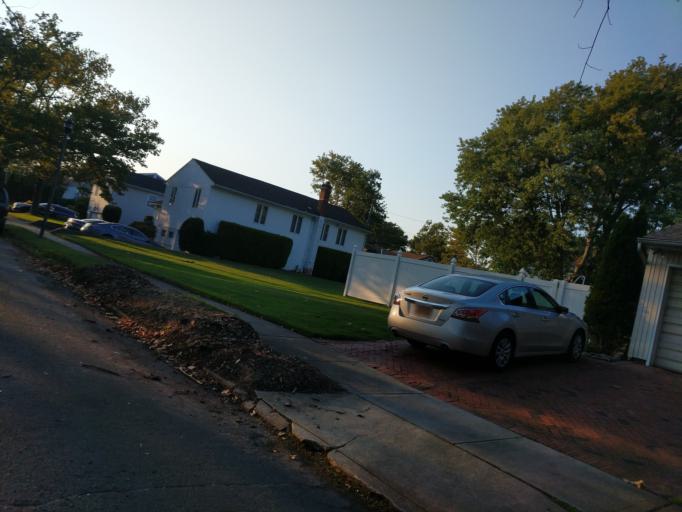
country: US
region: New York
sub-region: Nassau County
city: South Valley Stream
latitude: 40.6575
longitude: -73.7209
